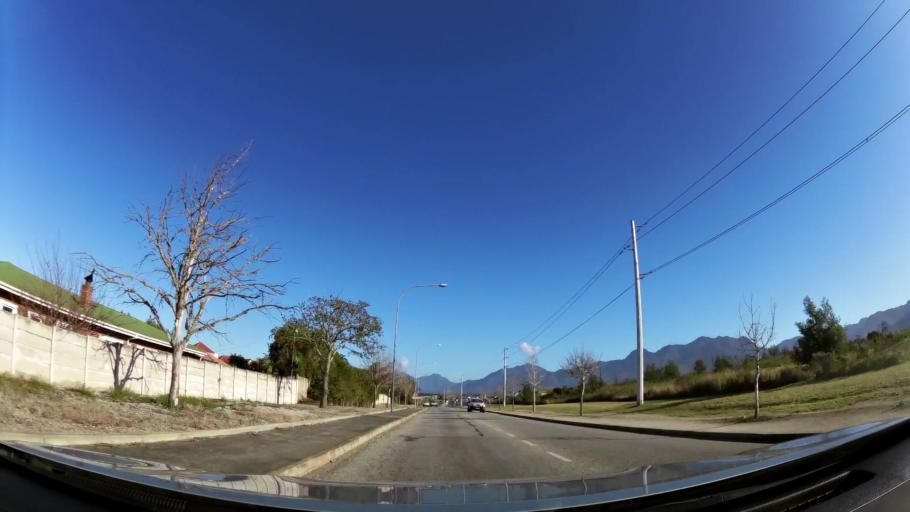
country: ZA
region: Western Cape
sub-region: Eden District Municipality
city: George
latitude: -33.9681
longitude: 22.4394
